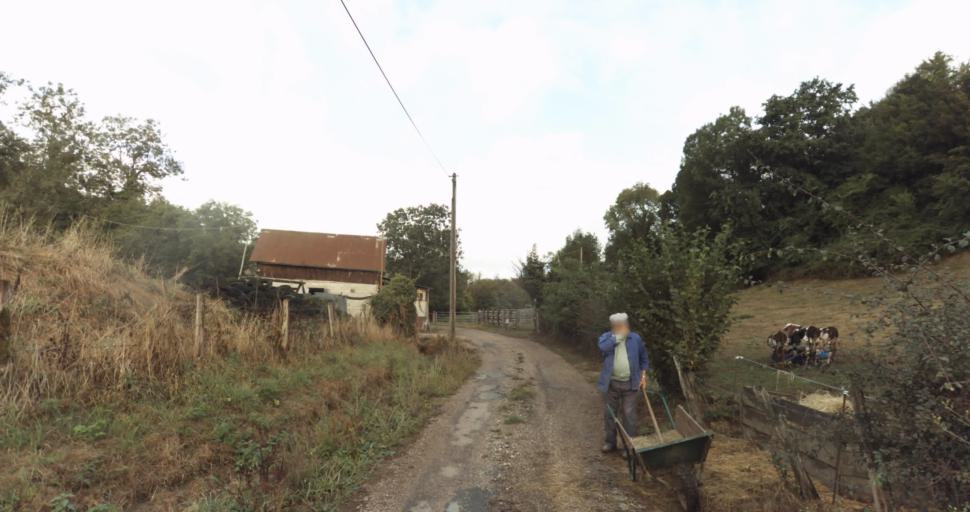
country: FR
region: Lower Normandy
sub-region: Departement de l'Orne
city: Vimoutiers
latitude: 48.8974
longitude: 0.2447
